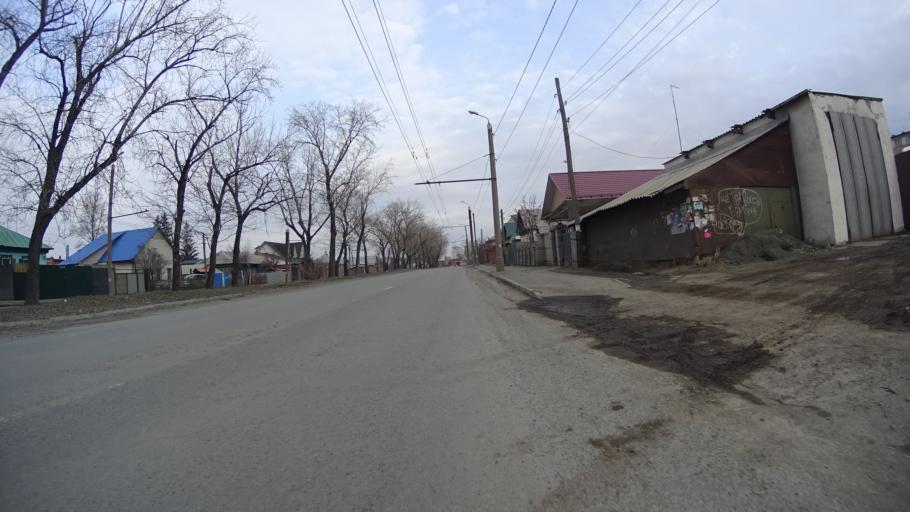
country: RU
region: Chelyabinsk
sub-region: Gorod Chelyabinsk
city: Chelyabinsk
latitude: 55.1915
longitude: 61.4717
